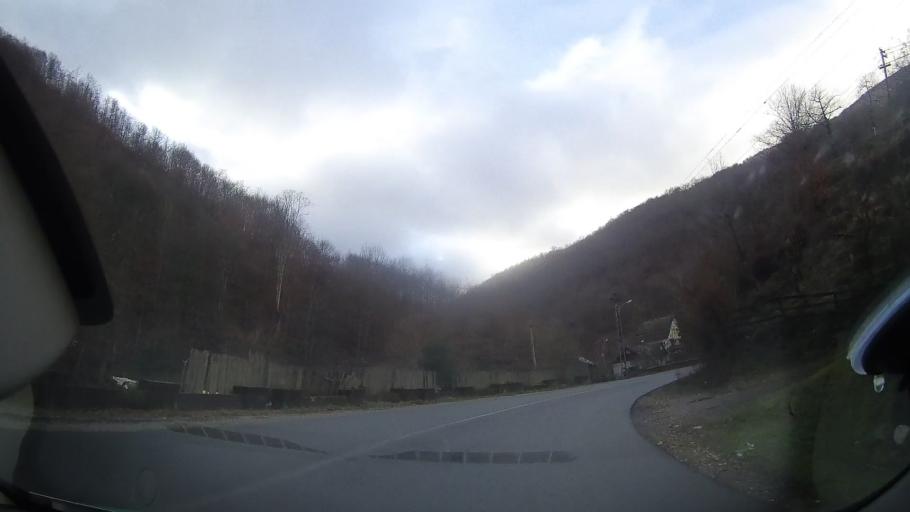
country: RO
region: Cluj
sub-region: Comuna Maguri-Racatau
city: Maguri-Racatau
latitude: 46.6770
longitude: 23.2599
